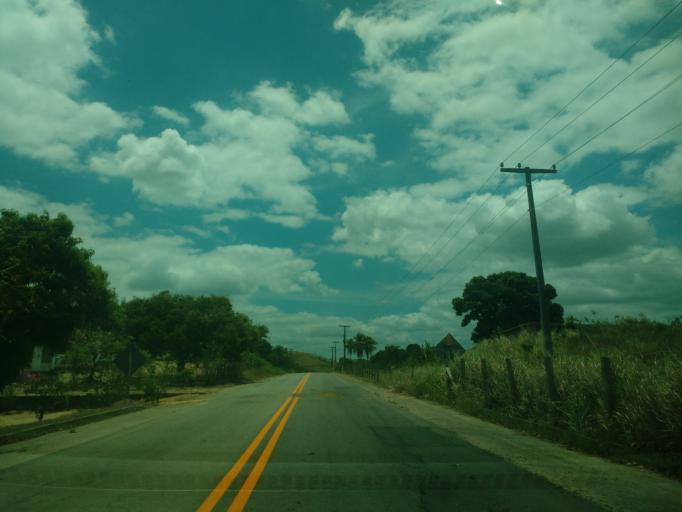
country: BR
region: Alagoas
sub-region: Uniao Dos Palmares
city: Uniao dos Palmares
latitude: -9.1420
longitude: -36.0477
